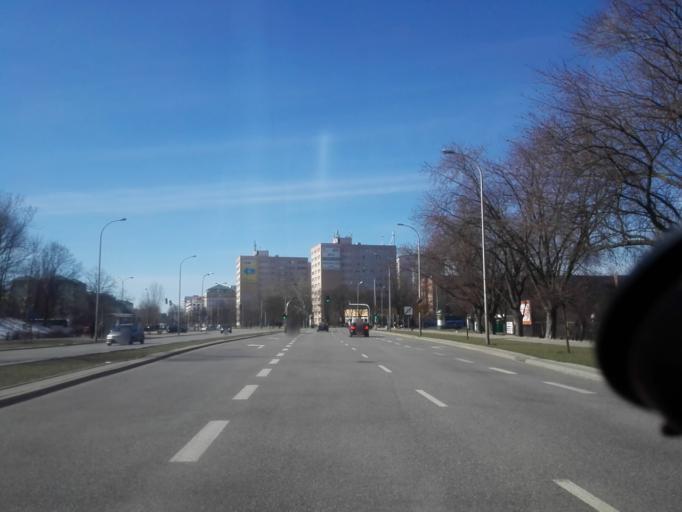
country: PL
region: Masovian Voivodeship
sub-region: Warszawa
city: Ochota
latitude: 52.1983
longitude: 20.9858
